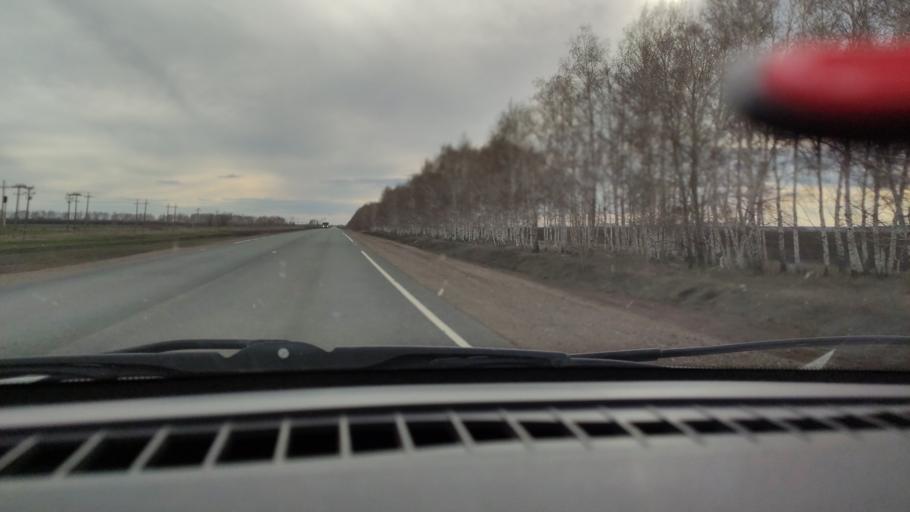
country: RU
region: Bashkortostan
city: Mayachnyy
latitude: 52.3767
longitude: 55.6372
